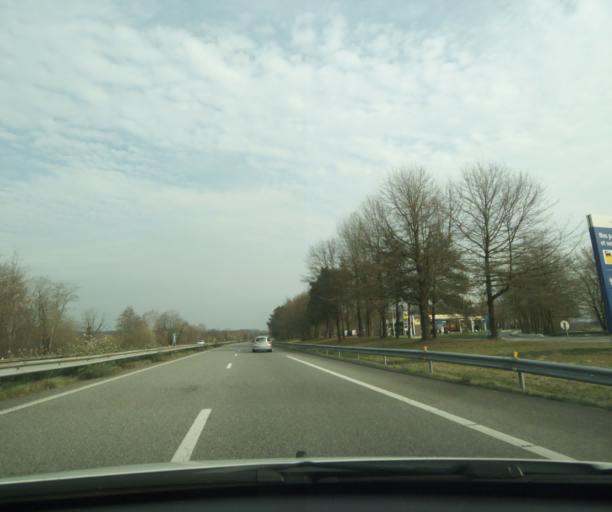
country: FR
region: Aquitaine
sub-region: Departement des Pyrenees-Atlantiques
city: Mourenx
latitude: 43.4225
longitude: -0.6005
